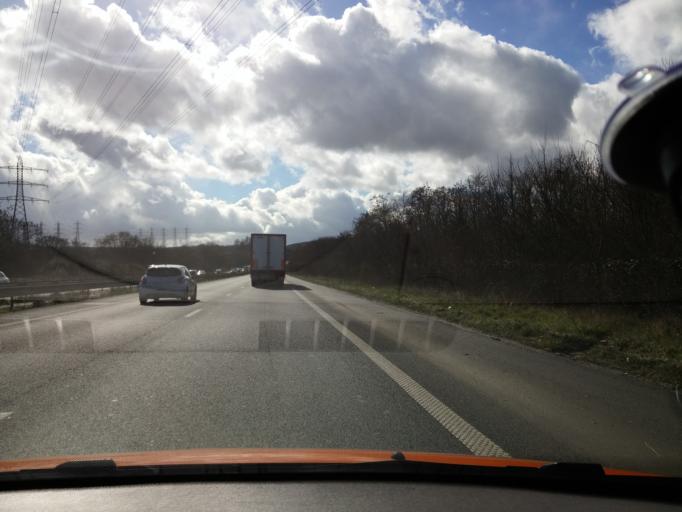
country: FR
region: Ile-de-France
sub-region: Departement de l'Essonne
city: Palaiseau
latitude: 48.7101
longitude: 2.2515
